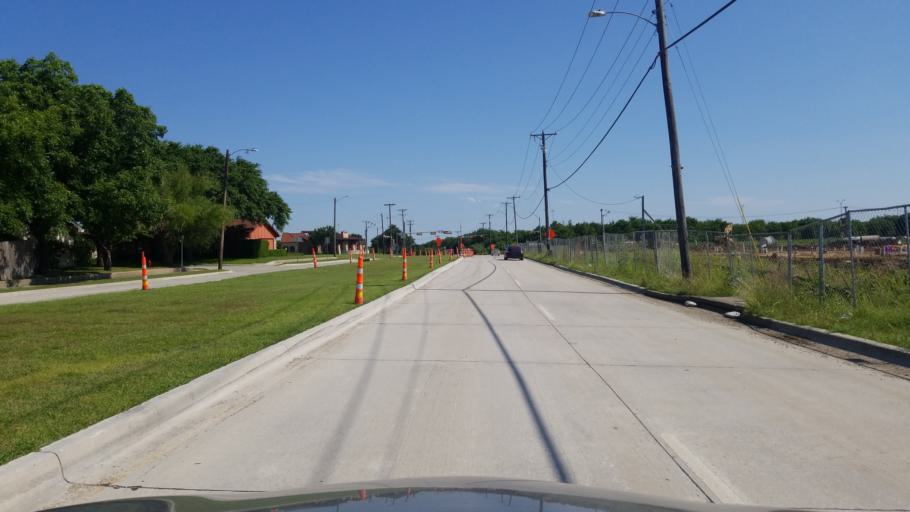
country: US
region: Texas
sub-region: Dallas County
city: Grand Prairie
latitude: 32.6831
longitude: -97.0192
